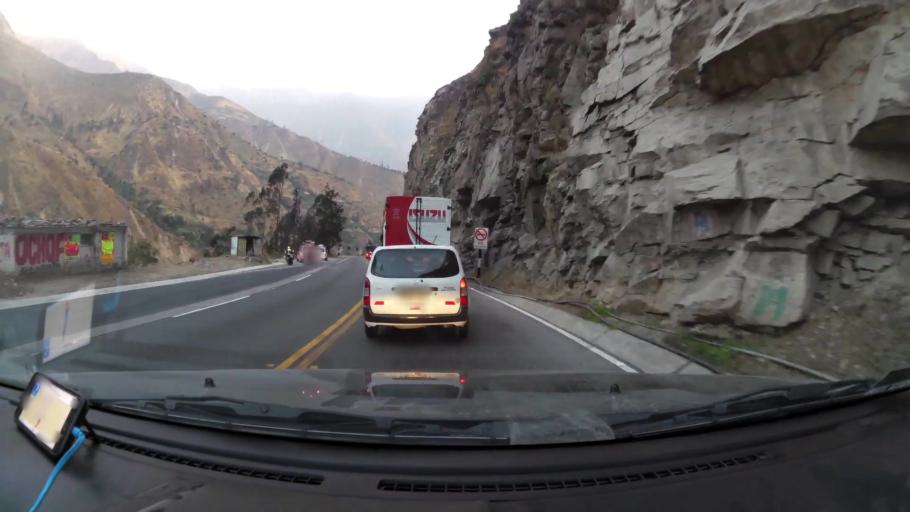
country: PE
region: Lima
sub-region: Provincia de Huarochiri
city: Surco
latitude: -11.8717
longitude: -76.4276
